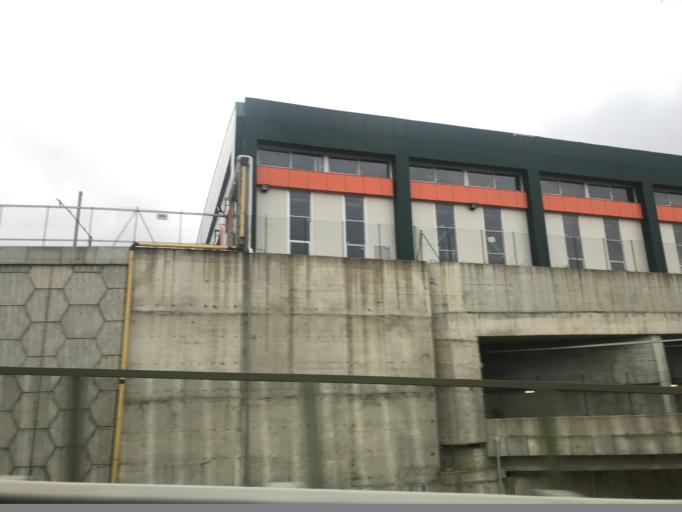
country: TR
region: Istanbul
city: Umraniye
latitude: 41.0364
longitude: 29.1516
